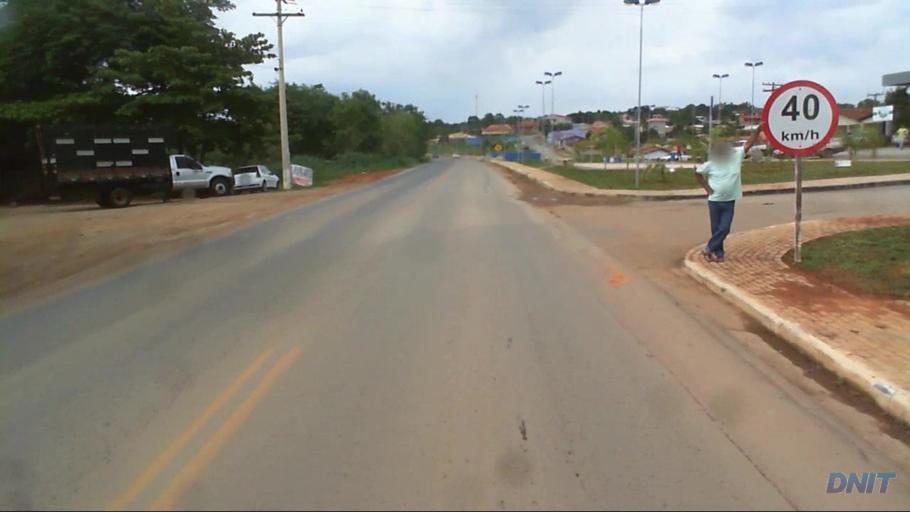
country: BR
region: Goias
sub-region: Padre Bernardo
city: Padre Bernardo
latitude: -15.1732
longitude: -48.2858
